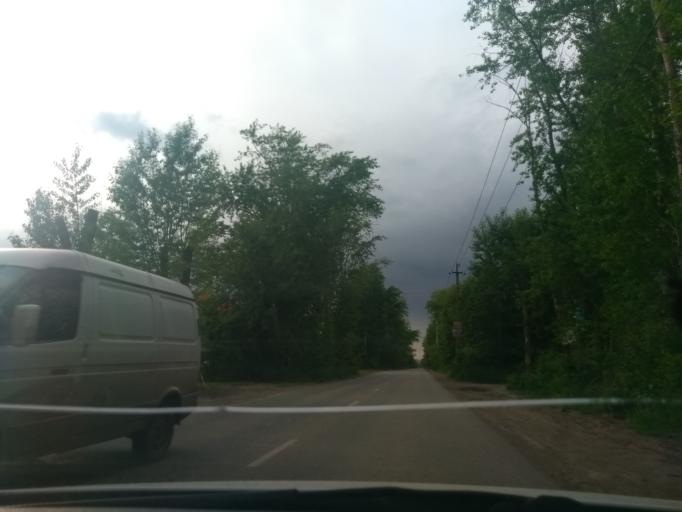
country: RU
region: Perm
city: Perm
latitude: 57.9981
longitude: 56.3351
